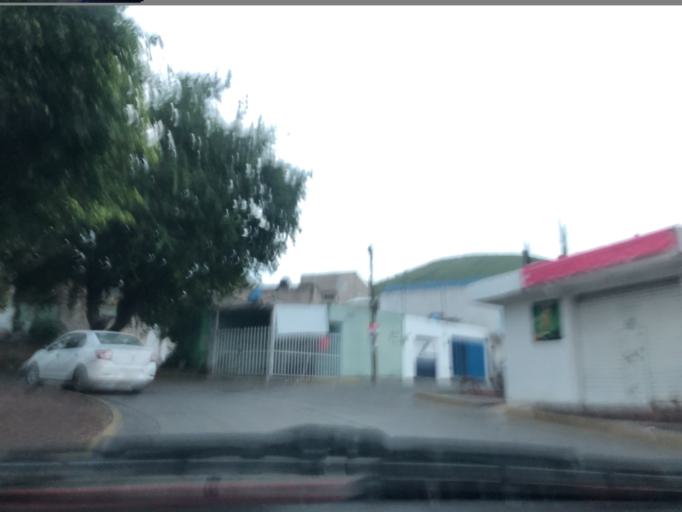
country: MX
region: Jalisco
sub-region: San Pedro Tlaquepaque
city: Paseo del Prado
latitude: 20.6141
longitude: -103.3918
